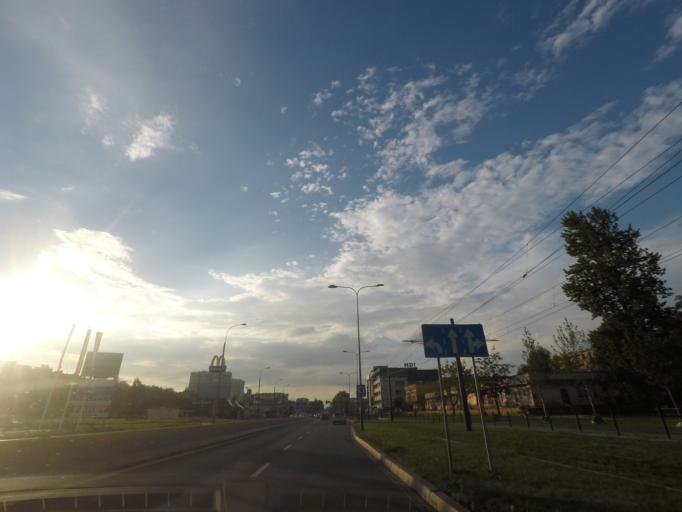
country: PL
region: Lesser Poland Voivodeship
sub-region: Krakow
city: Krakow
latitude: 50.0319
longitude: 19.9718
